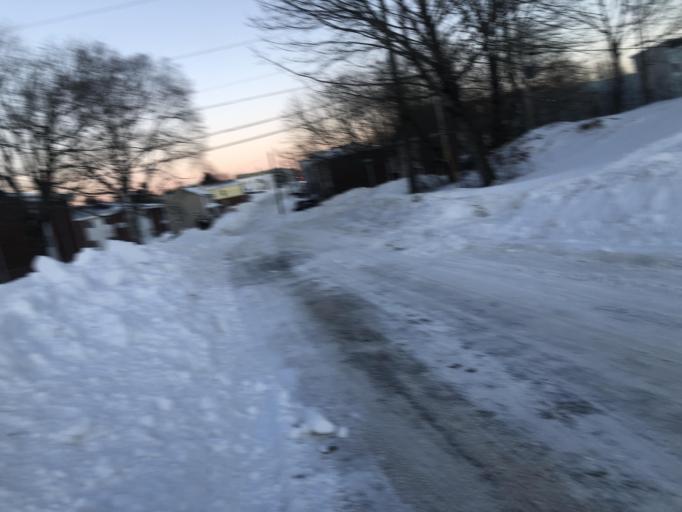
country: CA
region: New Brunswick
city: Saint John
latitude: 45.2774
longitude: -66.0854
